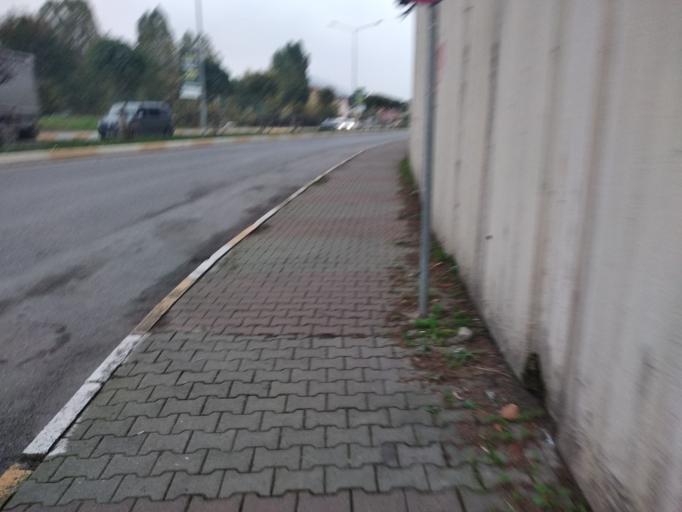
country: TR
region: Istanbul
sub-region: Atasehir
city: Atasehir
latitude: 40.9846
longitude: 29.1321
